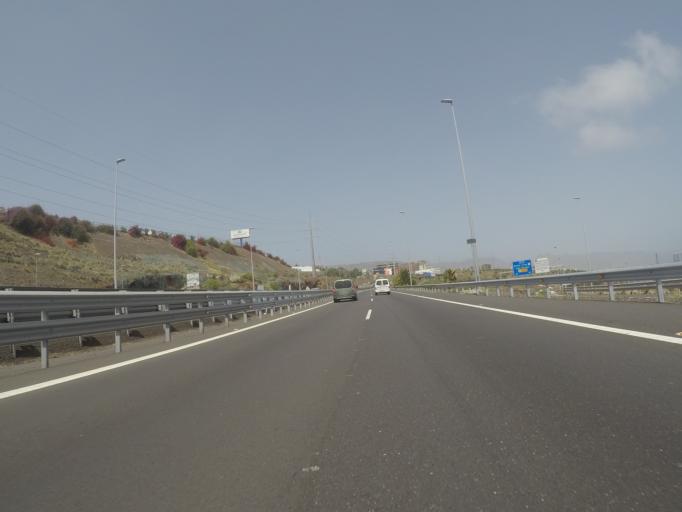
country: ES
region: Canary Islands
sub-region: Provincia de Santa Cruz de Tenerife
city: Santa Cruz de Tenerife
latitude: 28.4407
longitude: -16.2787
